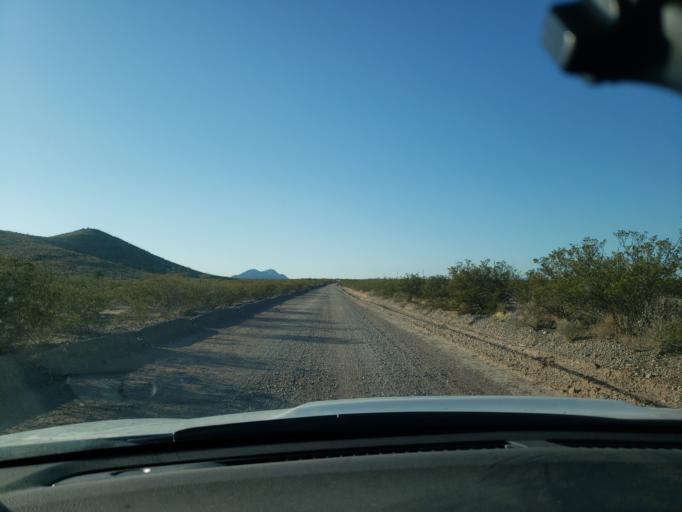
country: US
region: Texas
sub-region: Culberson County
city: Van Horn
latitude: 30.9652
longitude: -104.7748
